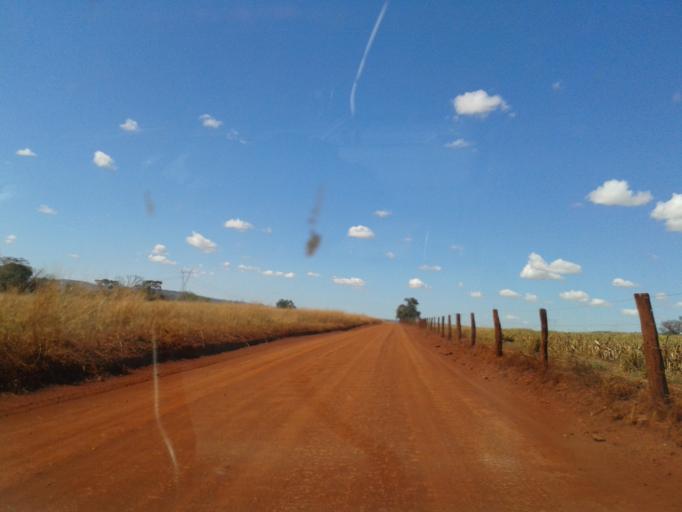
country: BR
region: Minas Gerais
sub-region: Centralina
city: Centralina
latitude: -18.5799
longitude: -49.1321
